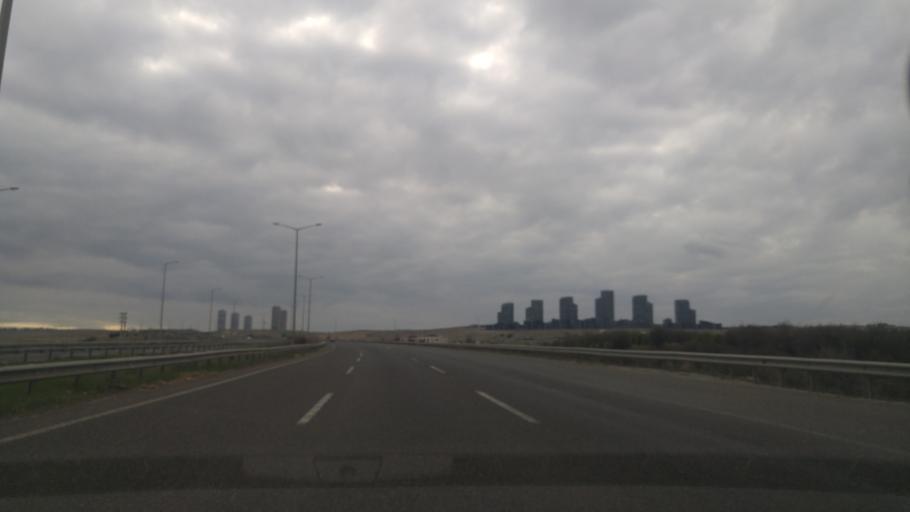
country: TR
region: Ankara
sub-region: Goelbasi
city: Golbasi
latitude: 39.7882
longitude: 32.7322
